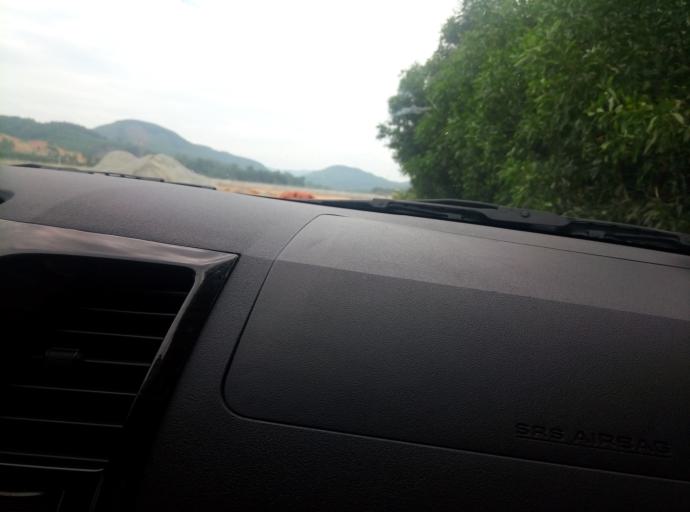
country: VN
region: Quang Nam
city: Tam Ky
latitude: 15.5305
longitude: 108.4767
